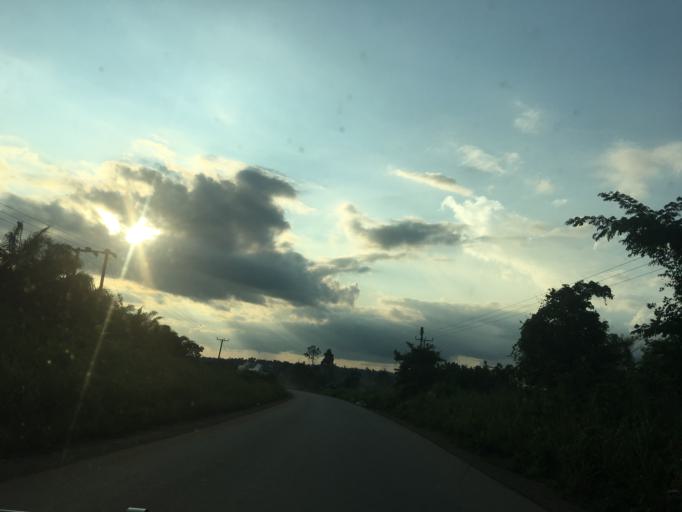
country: GH
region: Western
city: Bibiani
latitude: 6.6314
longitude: -2.4179
